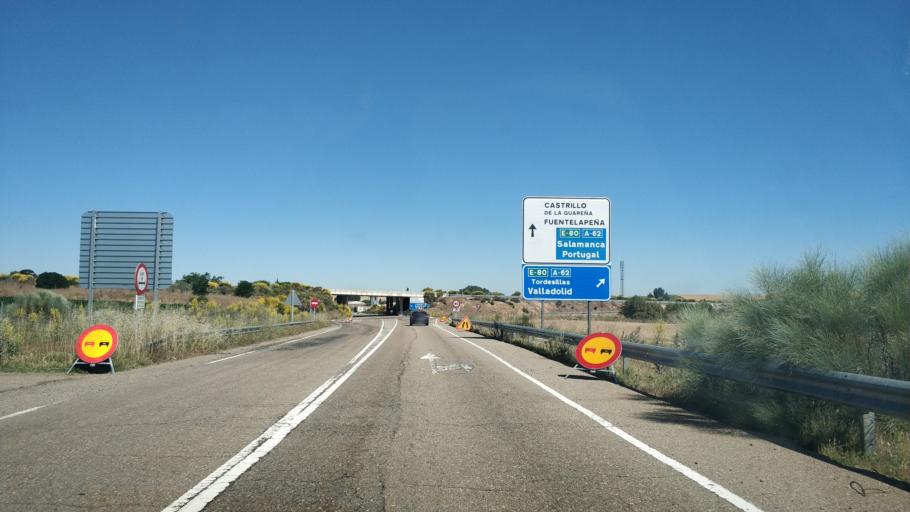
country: ES
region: Castille and Leon
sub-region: Provincia de Zamora
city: Castrillo de la Guarena
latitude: 41.2249
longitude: -5.3150
